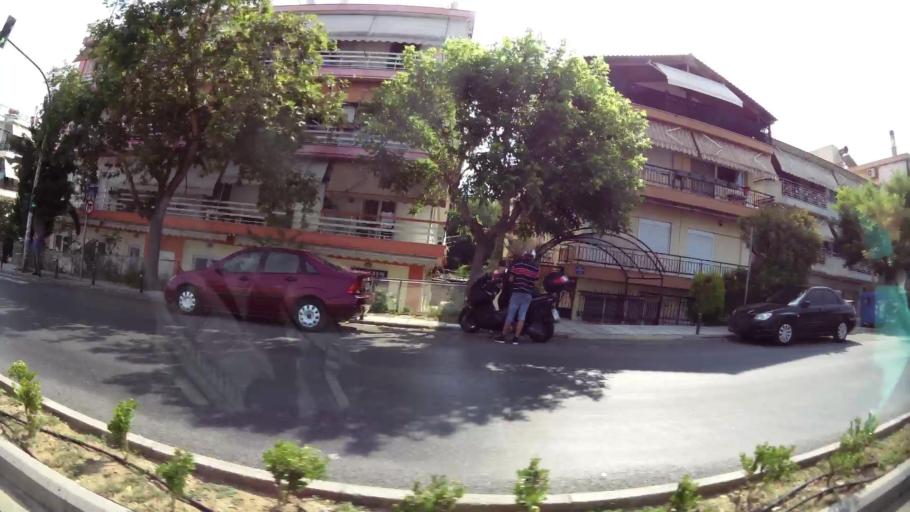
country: GR
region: Central Macedonia
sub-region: Nomos Thessalonikis
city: Agios Pavlos
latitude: 40.6456
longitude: 22.9628
